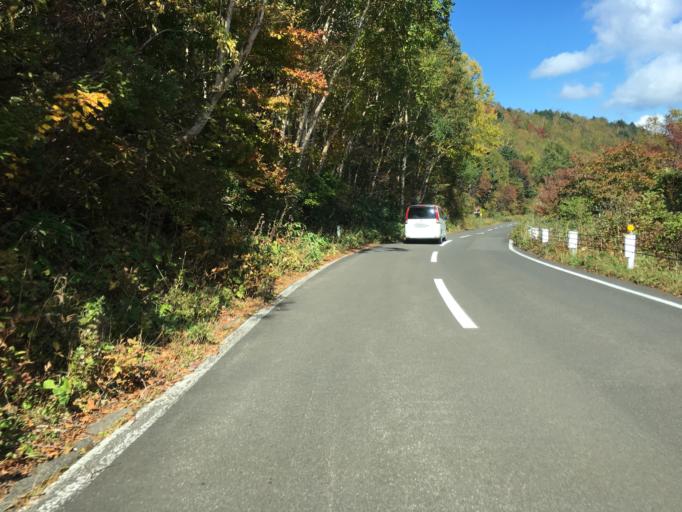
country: JP
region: Fukushima
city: Fukushima-shi
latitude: 37.7415
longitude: 140.2730
